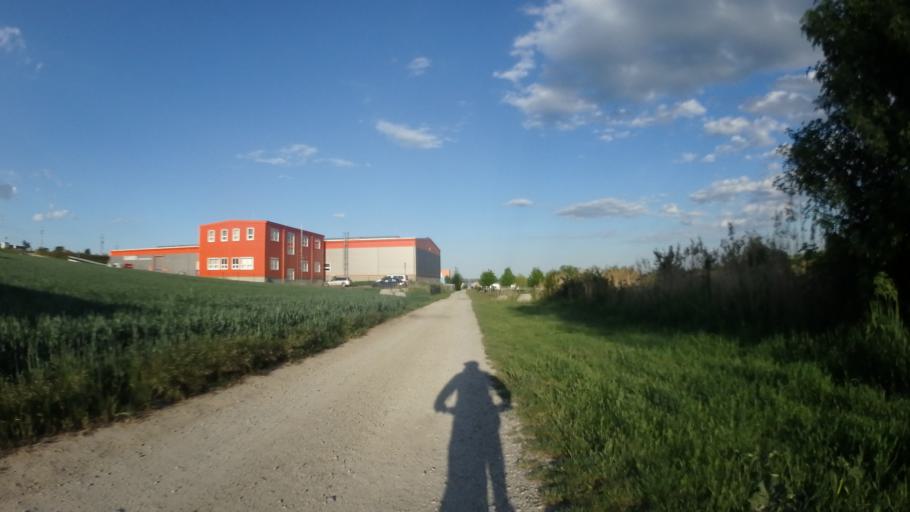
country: CZ
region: South Moravian
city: Moravany
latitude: 49.1437
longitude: 16.5892
